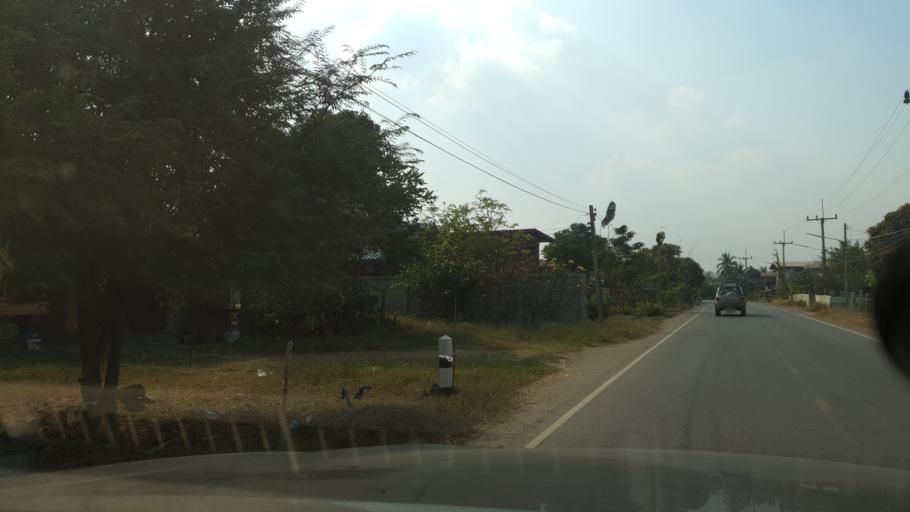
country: TH
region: Sukhothai
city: Ban Dan Lan Hoi
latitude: 17.1138
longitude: 99.5447
